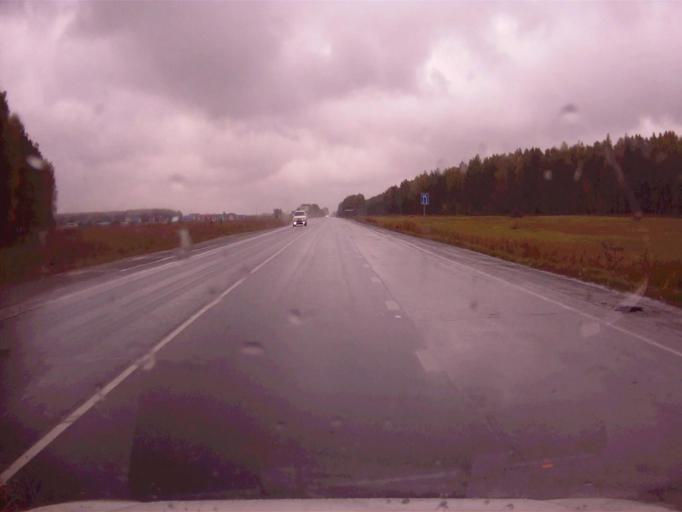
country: RU
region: Chelyabinsk
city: Argayash
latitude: 55.4186
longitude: 61.0219
